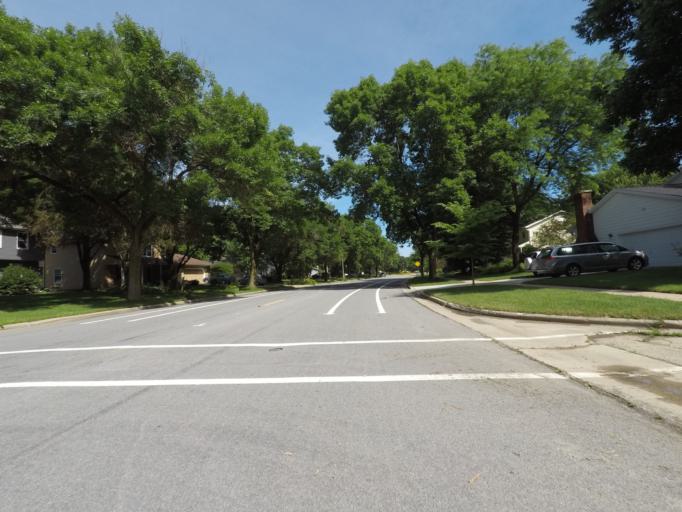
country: US
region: Wisconsin
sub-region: Dane County
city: Middleton
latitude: 43.0786
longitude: -89.5088
